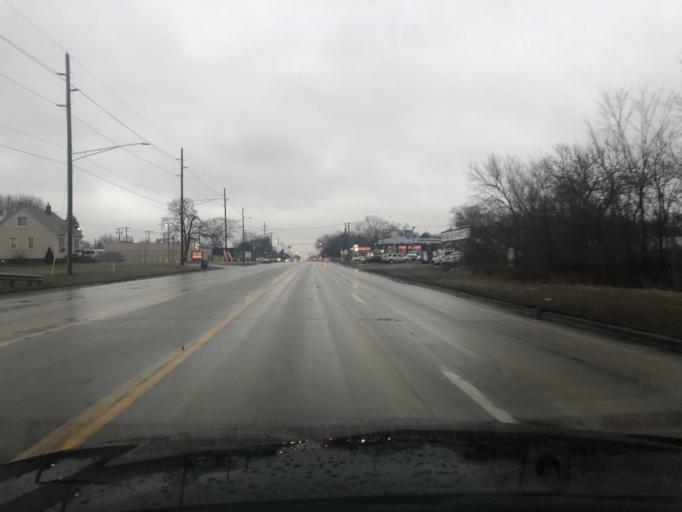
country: US
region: Michigan
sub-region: Wayne County
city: Inkster
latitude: 42.2682
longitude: -83.3115
